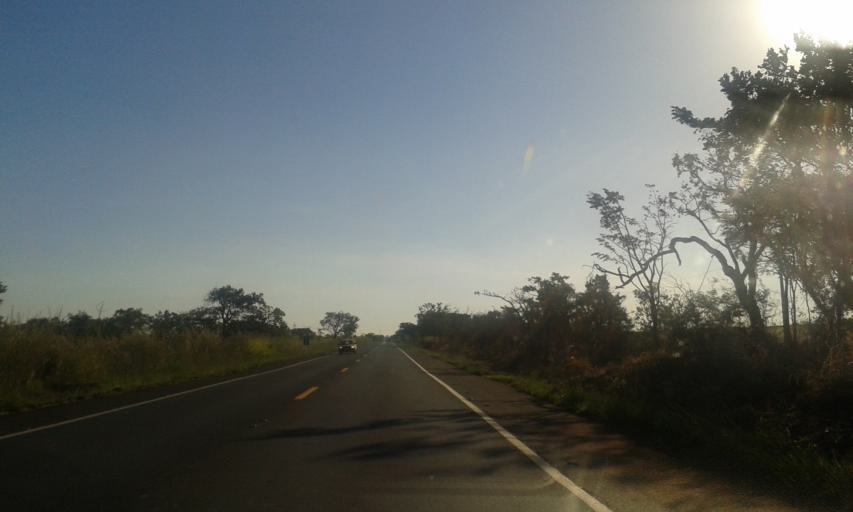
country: BR
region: Minas Gerais
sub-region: Monte Alegre De Minas
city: Monte Alegre de Minas
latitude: -18.8796
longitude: -49.1132
